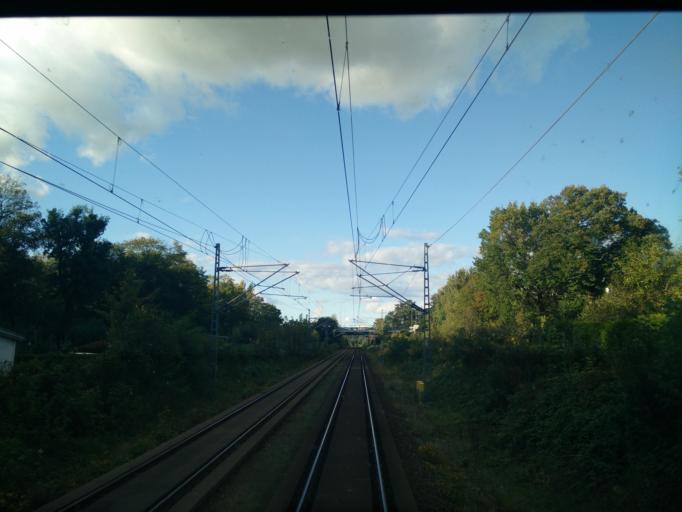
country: DE
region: Berlin
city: Westend
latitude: 52.5139
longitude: 13.2544
